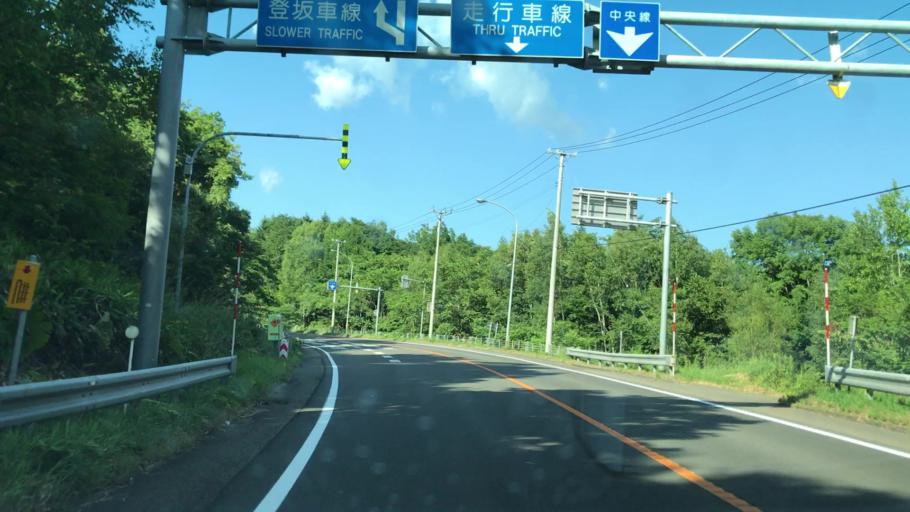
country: JP
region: Hokkaido
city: Shimo-furano
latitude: 42.8993
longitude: 142.4203
